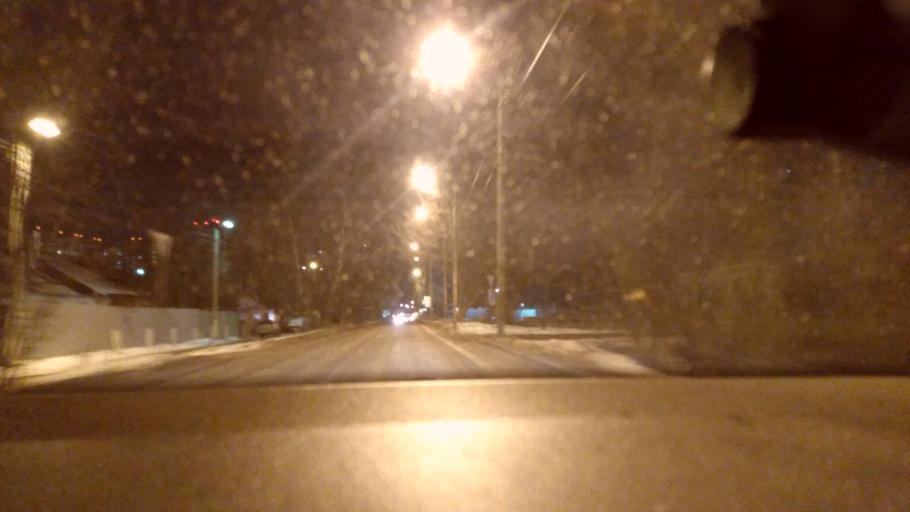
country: RU
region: Moskovskaya
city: Zheleznodorozhnyy
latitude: 55.7328
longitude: 38.0344
